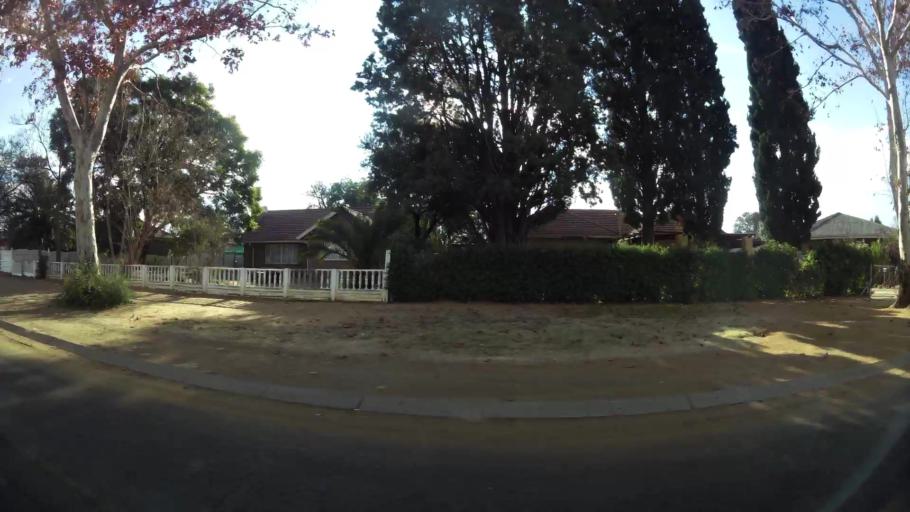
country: ZA
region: Orange Free State
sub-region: Lejweleputswa District Municipality
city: Welkom
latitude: -27.9905
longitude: 26.7514
